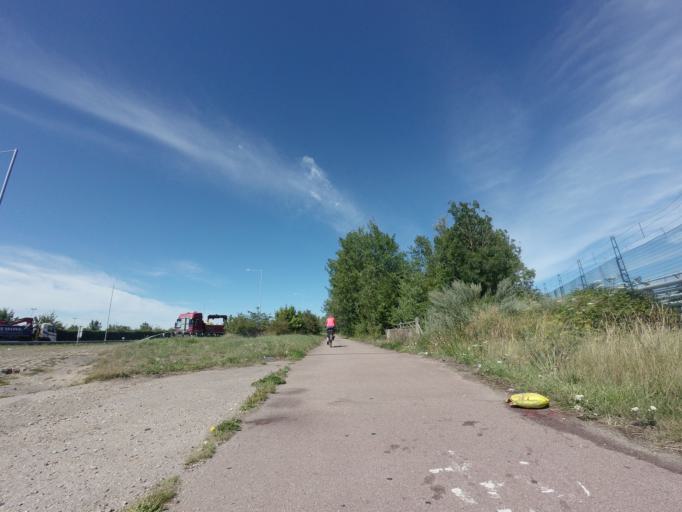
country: GB
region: England
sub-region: Kent
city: Sandwich
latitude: 51.2943
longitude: 1.3466
